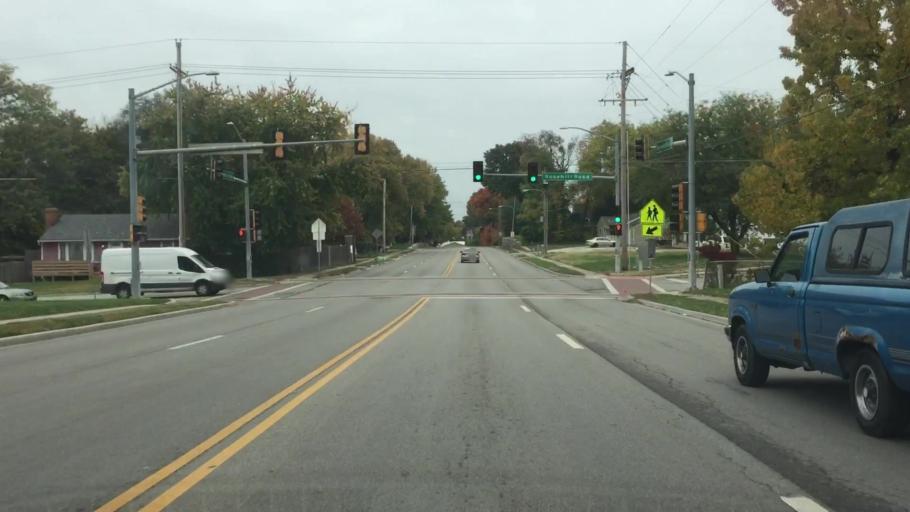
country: US
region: Kansas
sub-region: Johnson County
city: Shawnee
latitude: 39.0220
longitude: -94.7337
